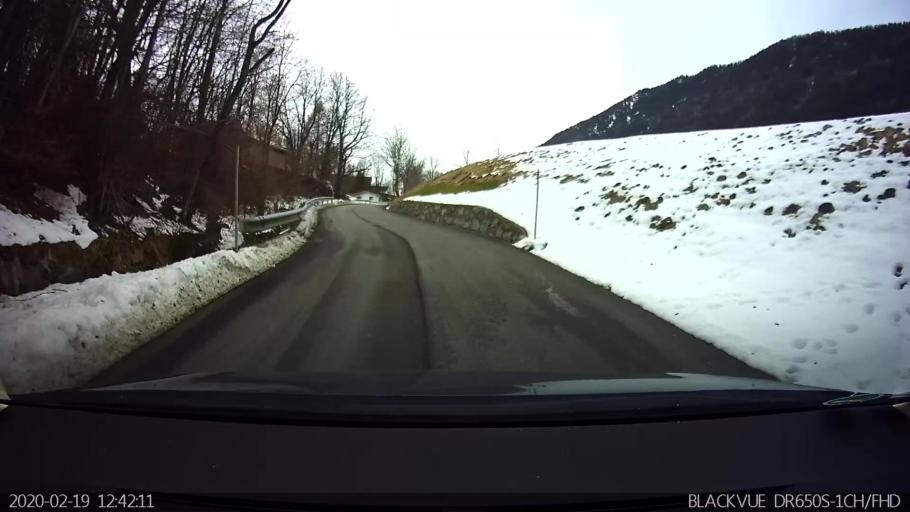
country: AT
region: Tyrol
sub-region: Politischer Bezirk Schwaz
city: Terfens
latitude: 47.3283
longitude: 11.6239
